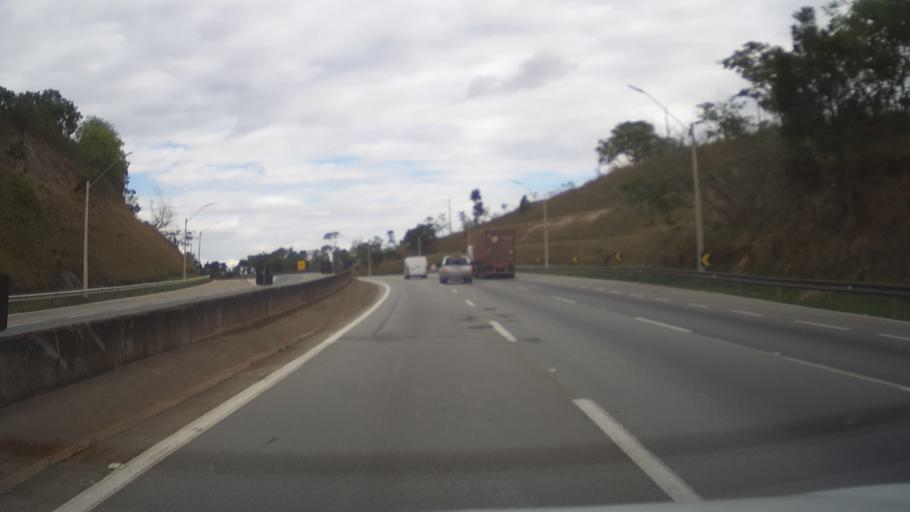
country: BR
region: Minas Gerais
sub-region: Itauna
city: Itauna
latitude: -20.3461
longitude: -44.4418
